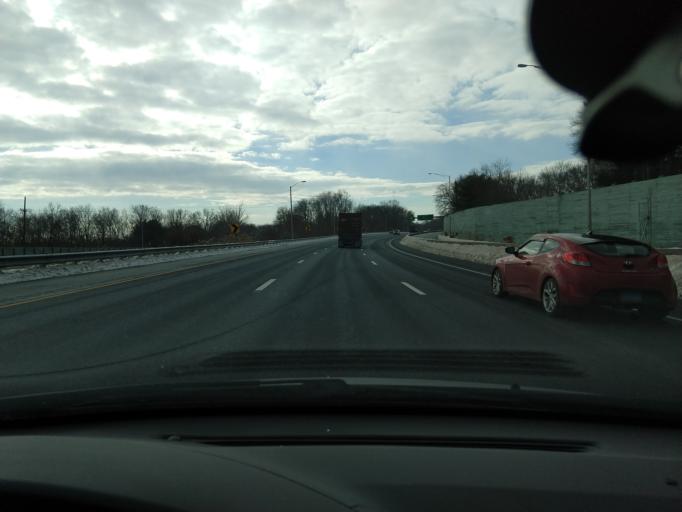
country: US
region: Connecticut
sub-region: New Haven County
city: Cheshire Village
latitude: 41.5842
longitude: -72.8997
